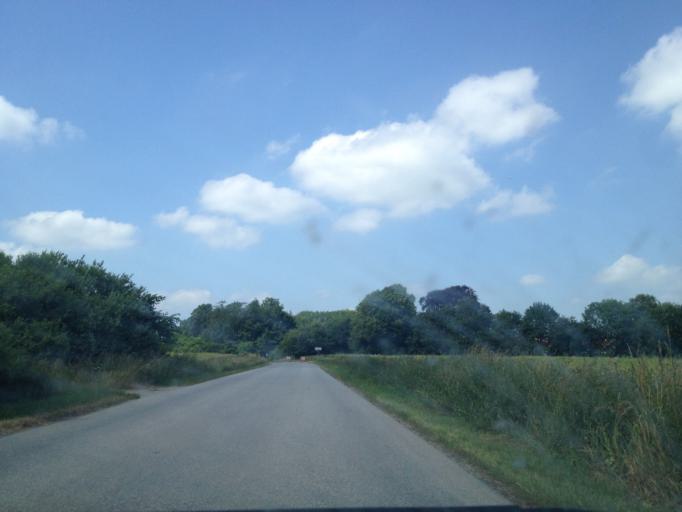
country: DK
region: South Denmark
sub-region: Kolding Kommune
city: Vamdrup
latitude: 55.3820
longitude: 9.2741
